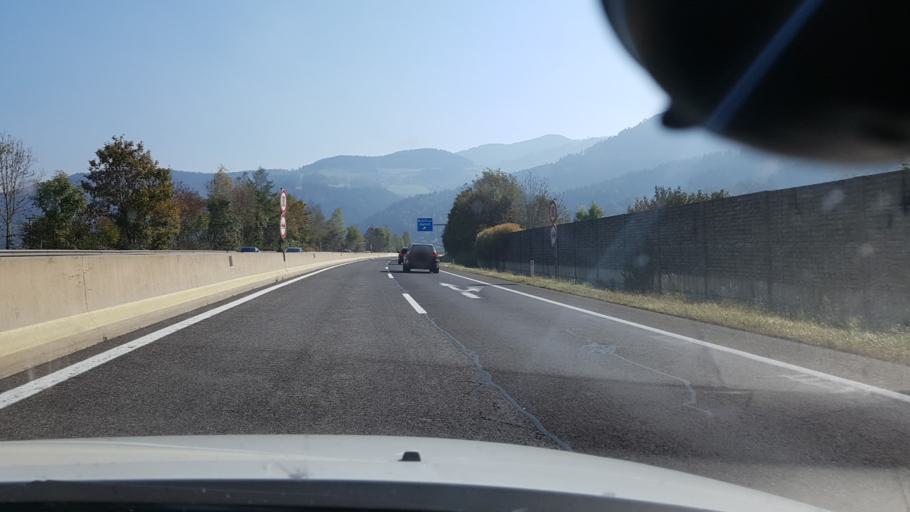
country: AT
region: Styria
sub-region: Politischer Bezirk Bruck-Muerzzuschlag
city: Oberaich
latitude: 47.4037
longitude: 15.2200
